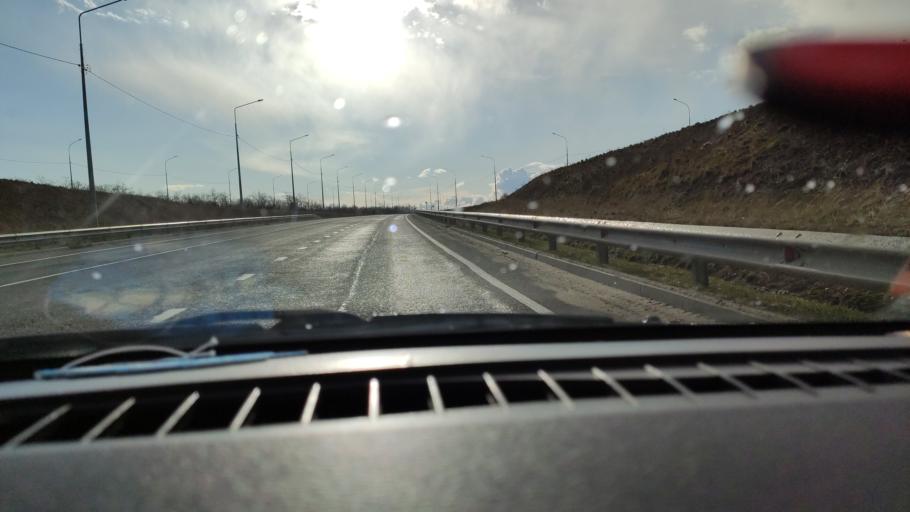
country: RU
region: Saratov
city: Yelshanka
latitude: 51.8197
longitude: 46.3541
